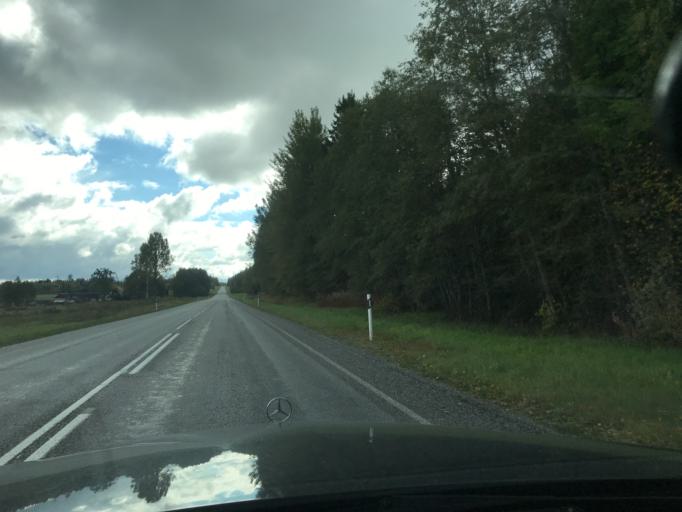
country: RU
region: Pskov
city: Pechory
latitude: 57.7106
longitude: 27.3210
